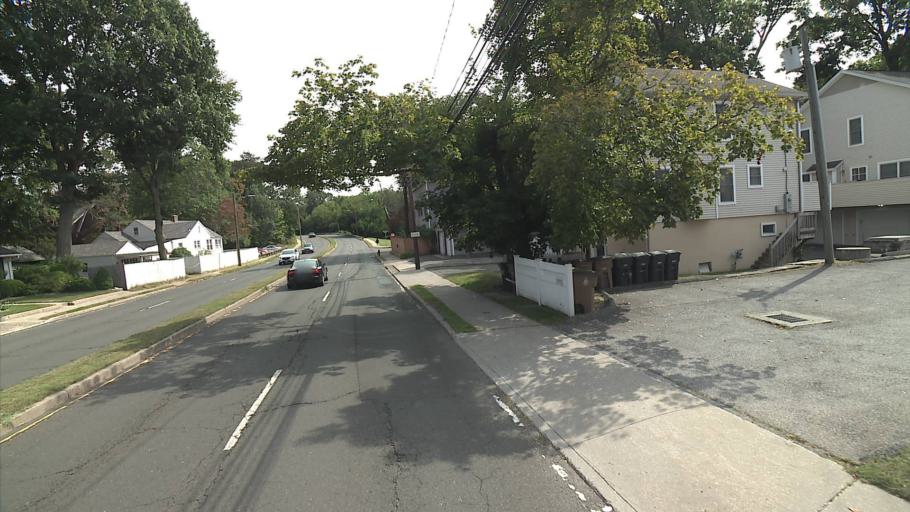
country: US
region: Connecticut
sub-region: Fairfield County
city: Stamford
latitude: 41.0686
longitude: -73.5526
